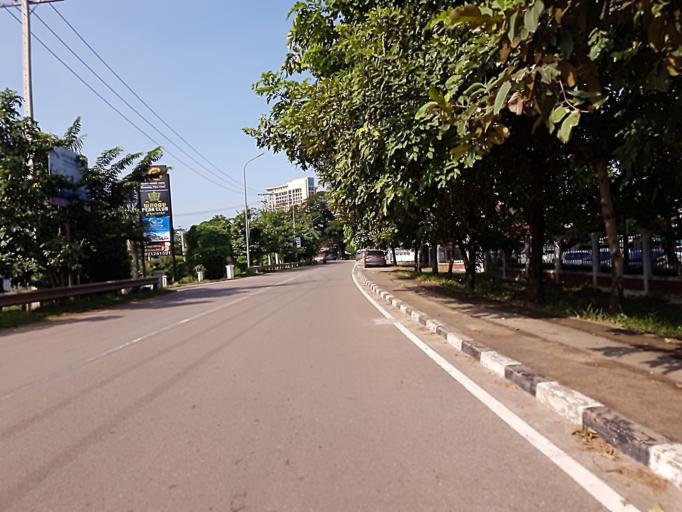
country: LA
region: Vientiane
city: Vientiane
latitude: 17.9453
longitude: 102.6211
